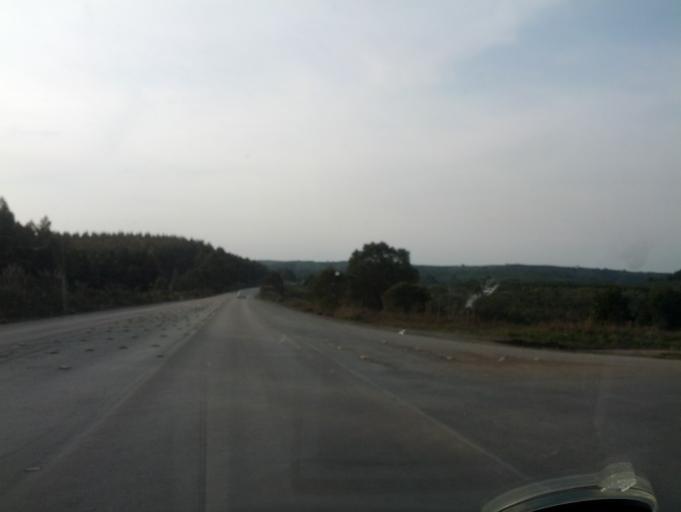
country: BR
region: Santa Catarina
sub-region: Otacilio Costa
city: Otacilio Costa
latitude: -27.4714
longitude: -50.1213
